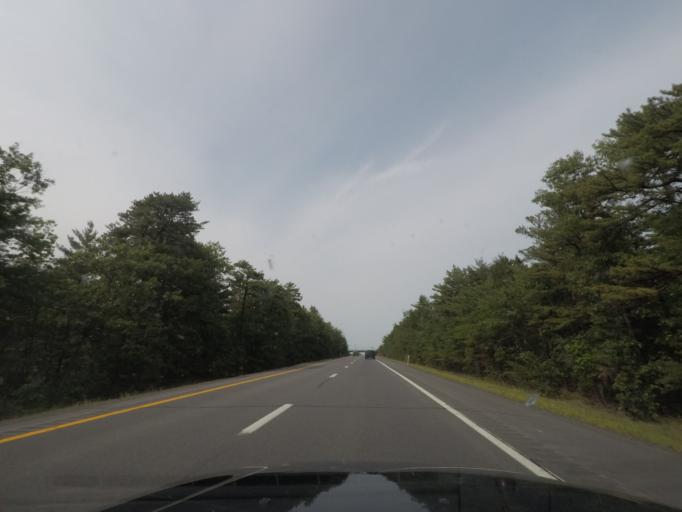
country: US
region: New York
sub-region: Essex County
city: Keeseville
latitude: 44.5129
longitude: -73.4988
